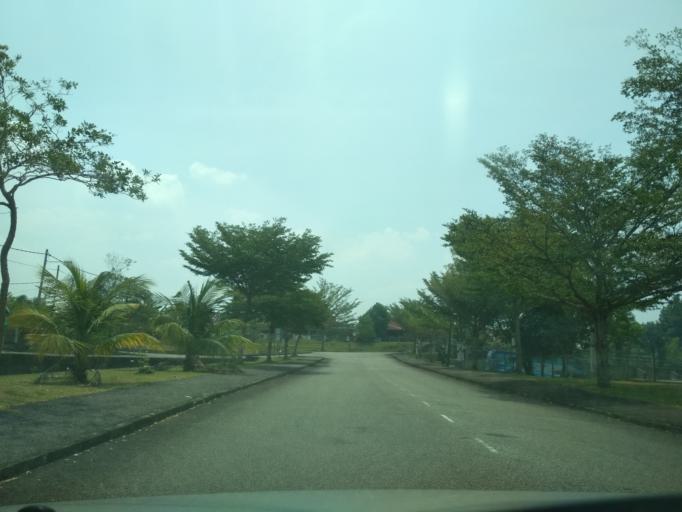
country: MY
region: Kedah
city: Kulim
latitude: 5.3608
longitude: 100.5335
